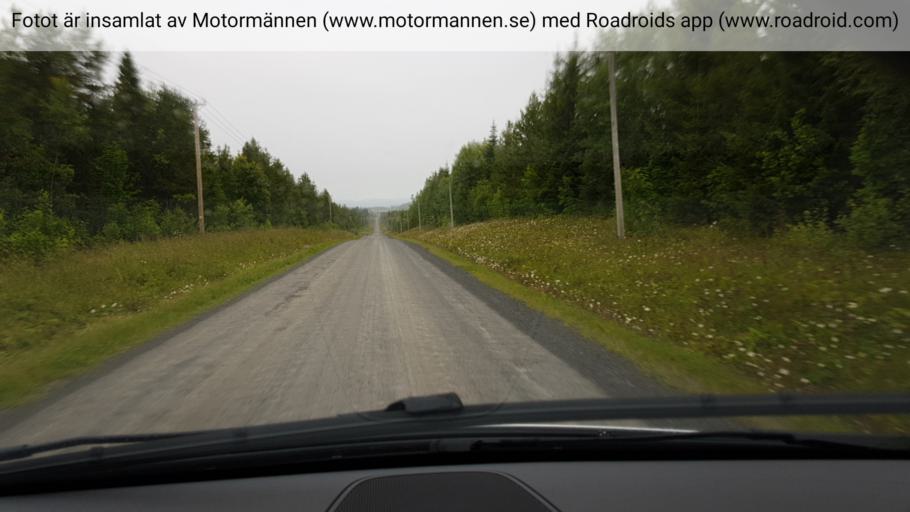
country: SE
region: Jaemtland
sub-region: OEstersunds Kommun
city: Lit
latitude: 63.6179
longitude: 14.9838
